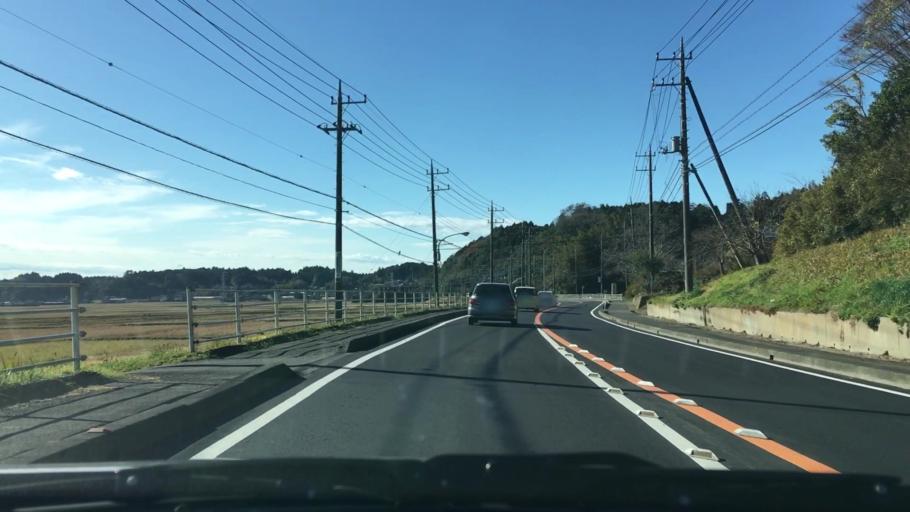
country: JP
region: Chiba
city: Omigawa
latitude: 35.8486
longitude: 140.5789
